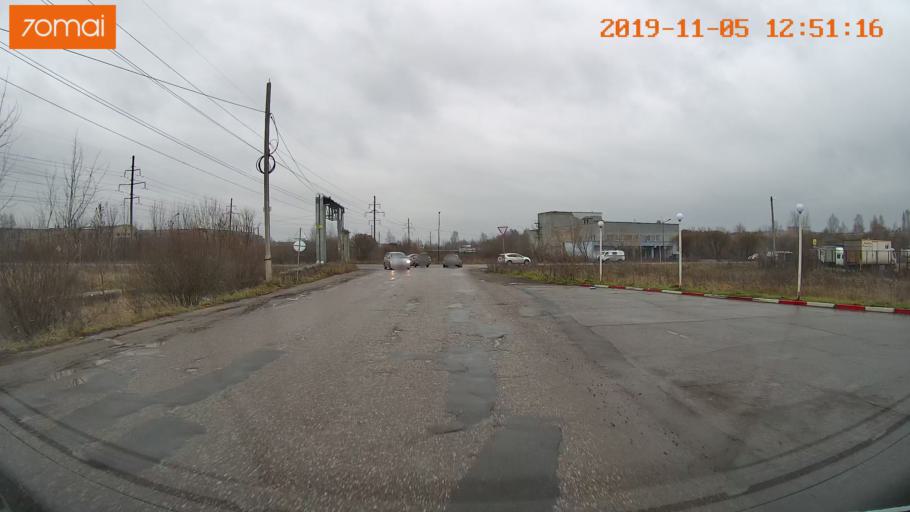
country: RU
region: Ivanovo
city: Kokhma
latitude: 56.9434
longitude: 41.1137
